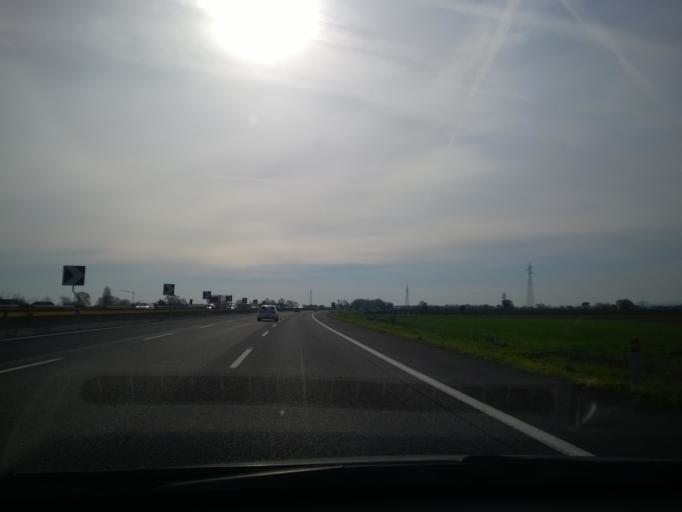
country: IT
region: Emilia-Romagna
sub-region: Forli-Cesena
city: Forli
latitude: 44.2804
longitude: 12.0195
